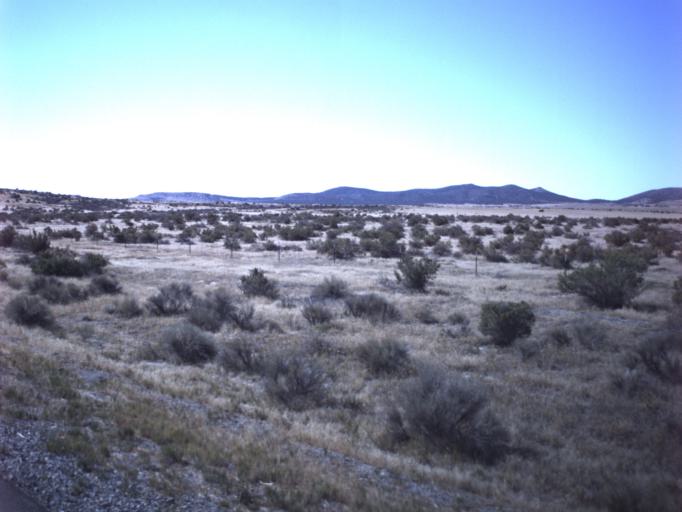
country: US
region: Utah
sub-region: Tooele County
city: Grantsville
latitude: 40.2955
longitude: -112.7426
